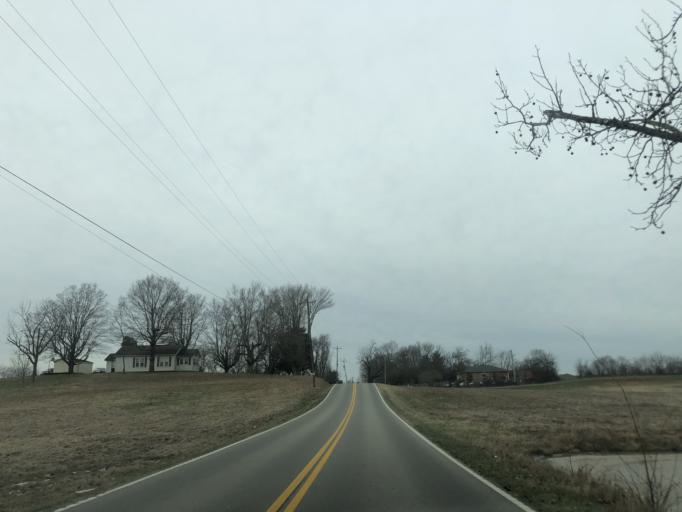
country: US
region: Tennessee
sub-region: Robertson County
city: Ridgetop
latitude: 36.3954
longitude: -86.7838
